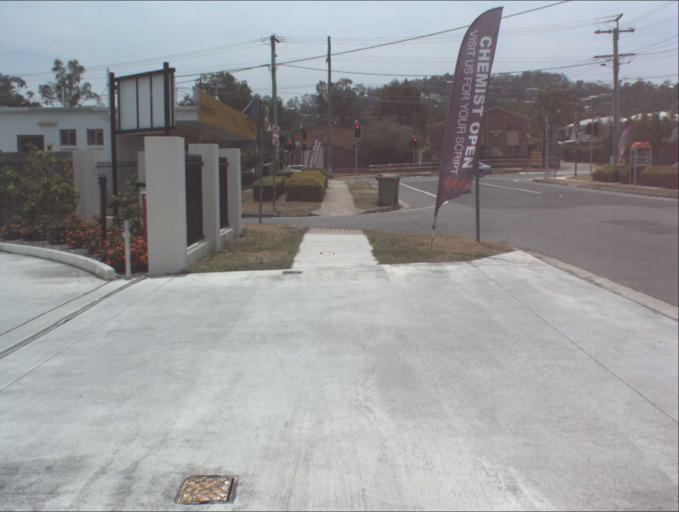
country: AU
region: Queensland
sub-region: Logan
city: Slacks Creek
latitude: -27.6661
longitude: 153.1856
